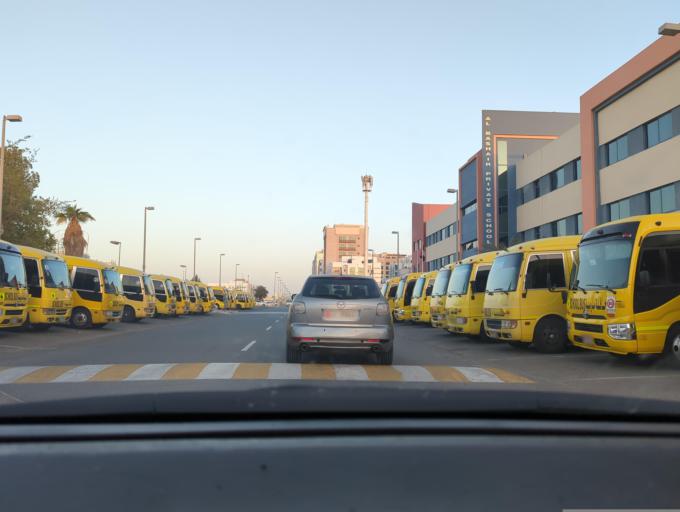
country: AE
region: Abu Dhabi
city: Abu Dhabi
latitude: 24.3204
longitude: 54.5336
